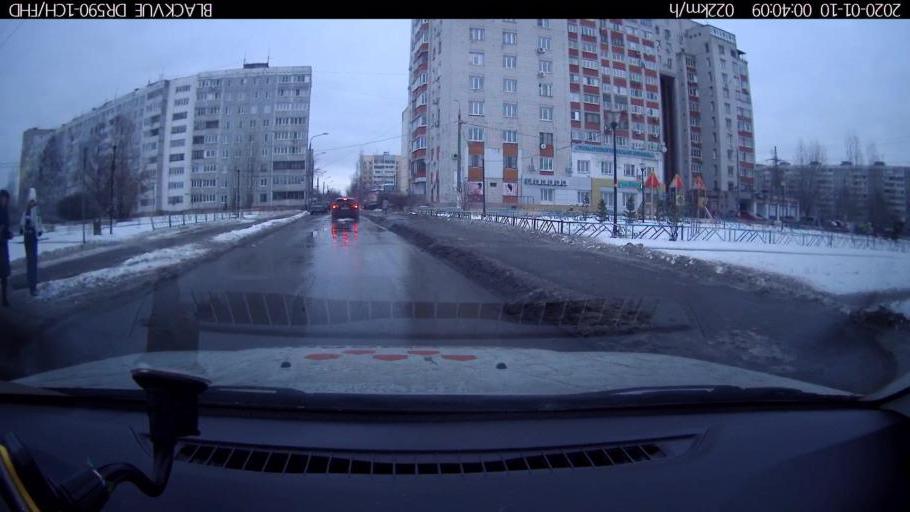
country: RU
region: Nizjnij Novgorod
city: Nizhniy Novgorod
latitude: 56.3300
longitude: 43.8666
